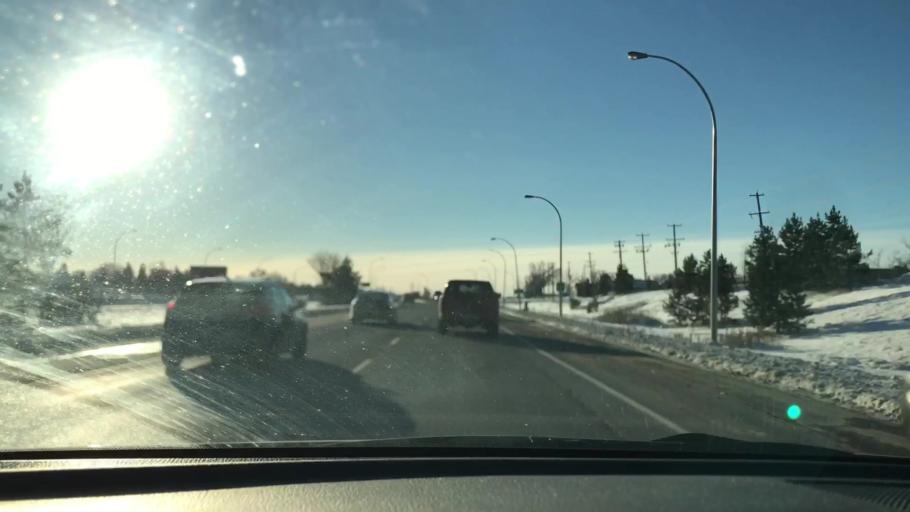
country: CA
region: Alberta
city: Edmonton
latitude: 53.4768
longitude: -113.4669
